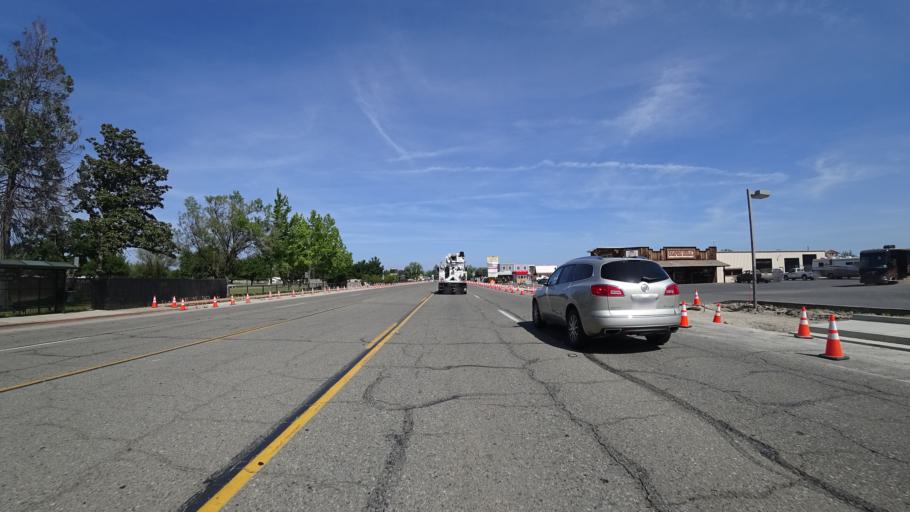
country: US
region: California
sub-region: Tehama County
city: Red Bluff
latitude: 40.1859
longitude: -122.2037
